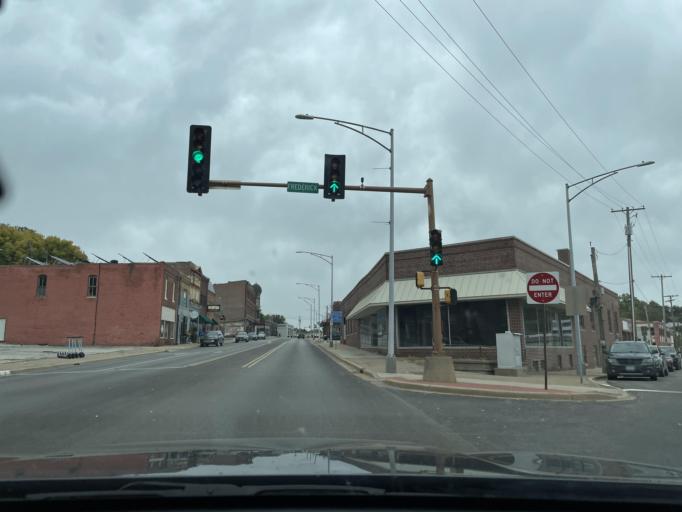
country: US
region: Missouri
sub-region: Buchanan County
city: Saint Joseph
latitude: 39.7691
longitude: -94.8467
